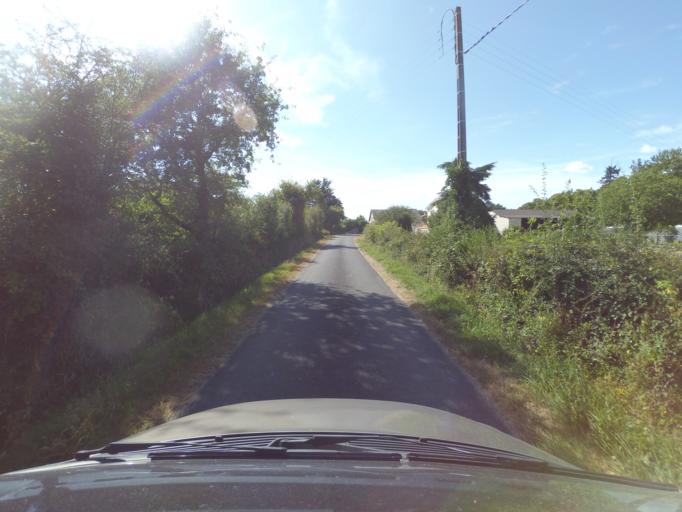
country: FR
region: Pays de la Loire
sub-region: Departement de la Loire-Atlantique
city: Le Bignon
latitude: 47.0910
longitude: -1.4706
